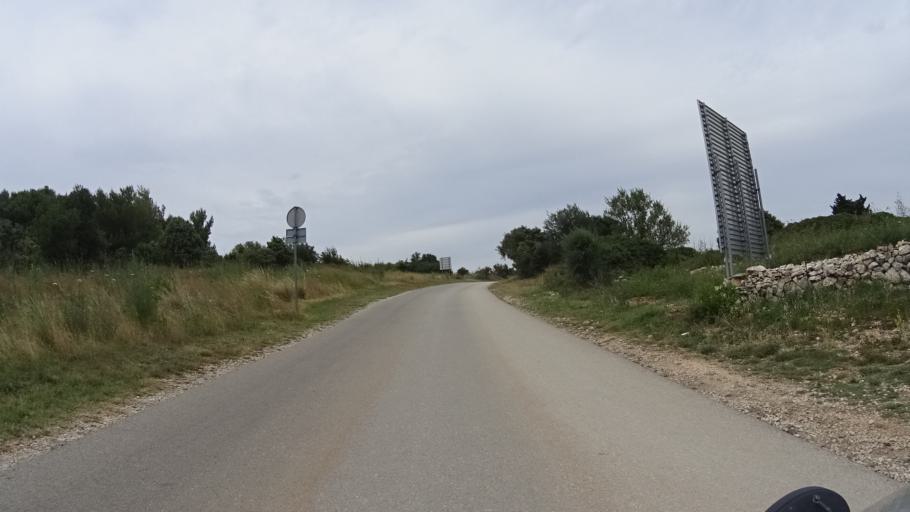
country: HR
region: Istarska
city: Medulin
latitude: 44.7986
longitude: 13.9060
